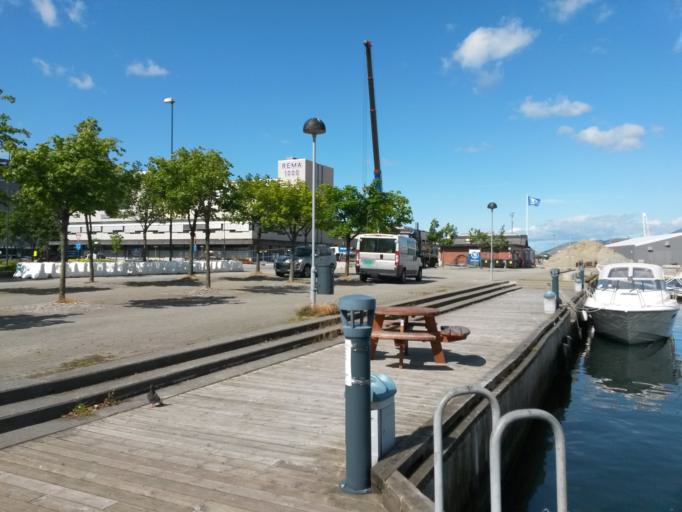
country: NO
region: Rogaland
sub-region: Sandnes
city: Sandnes
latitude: 58.8521
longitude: 5.7405
